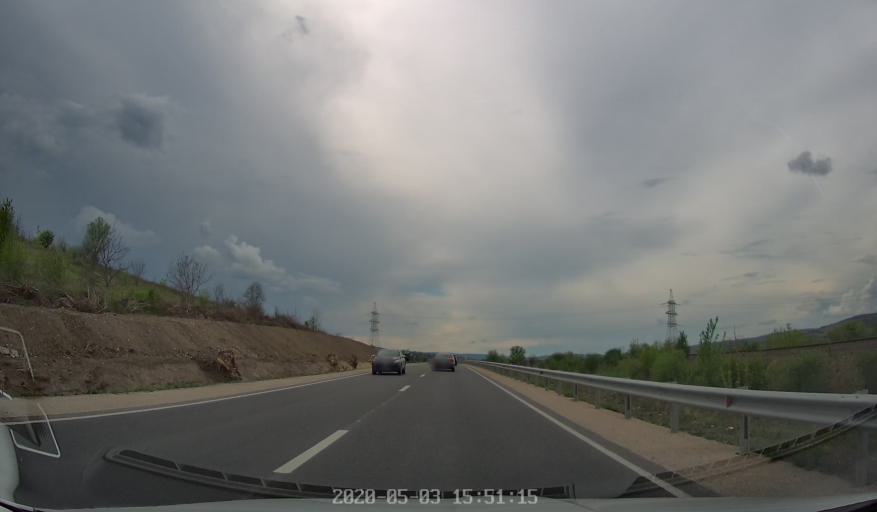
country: MD
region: Straseni
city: Straseni
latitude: 47.1605
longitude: 28.5624
